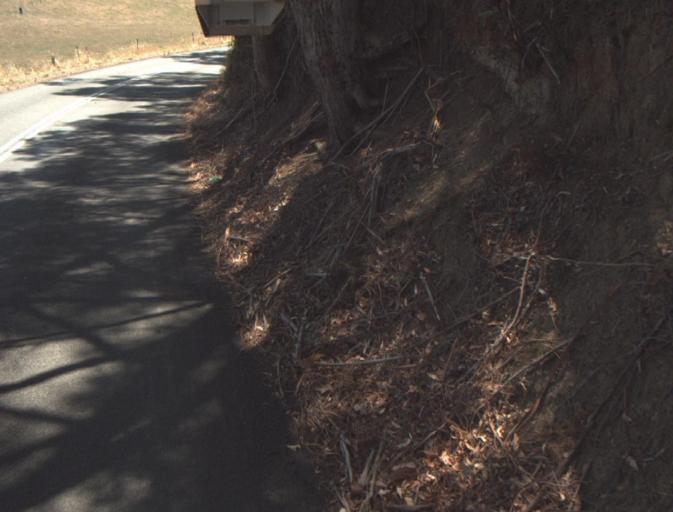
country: AU
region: Tasmania
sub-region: Launceston
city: Mayfield
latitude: -41.2680
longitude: 147.1288
